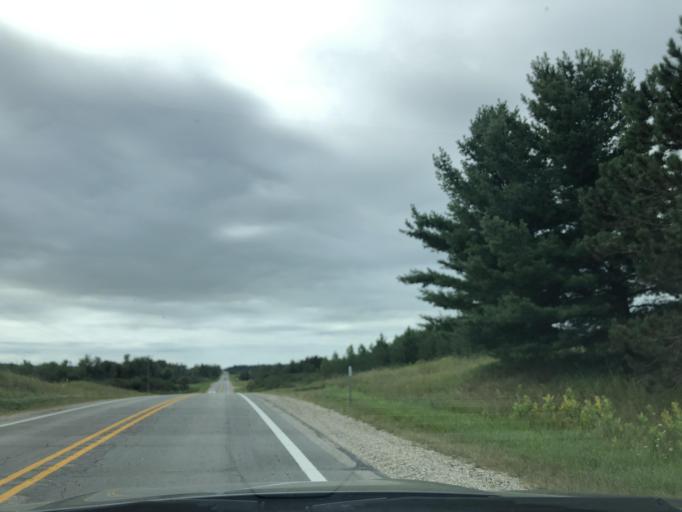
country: US
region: Michigan
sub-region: Missaukee County
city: Lake City
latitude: 44.2328
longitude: -85.2150
